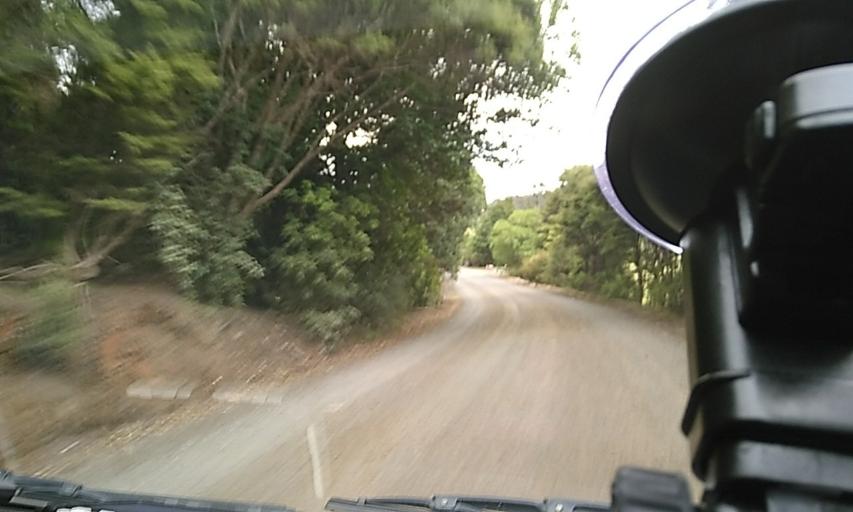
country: NZ
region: Northland
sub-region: Kaipara District
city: Dargaville
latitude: -35.6527
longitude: 173.5593
